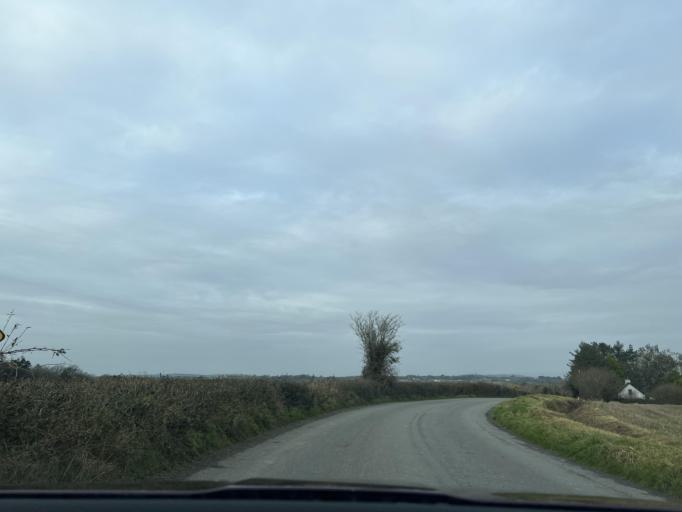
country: IE
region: Leinster
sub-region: Loch Garman
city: Castlebridge
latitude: 52.3796
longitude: -6.5468
